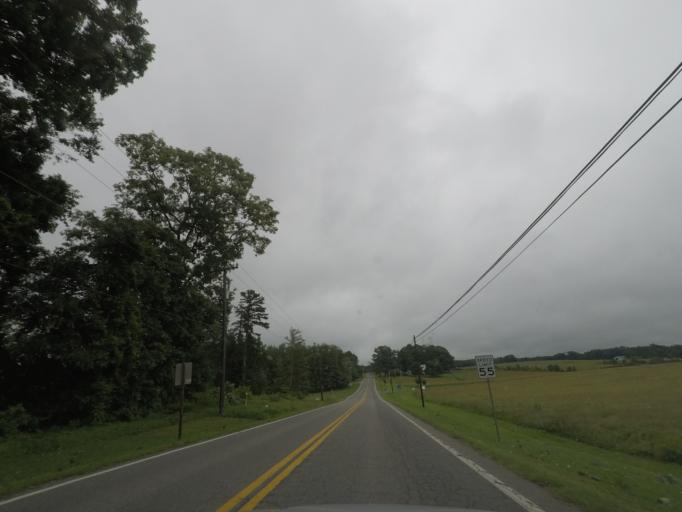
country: US
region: Virginia
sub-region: Fluvanna County
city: Weber City
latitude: 37.7703
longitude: -78.2546
